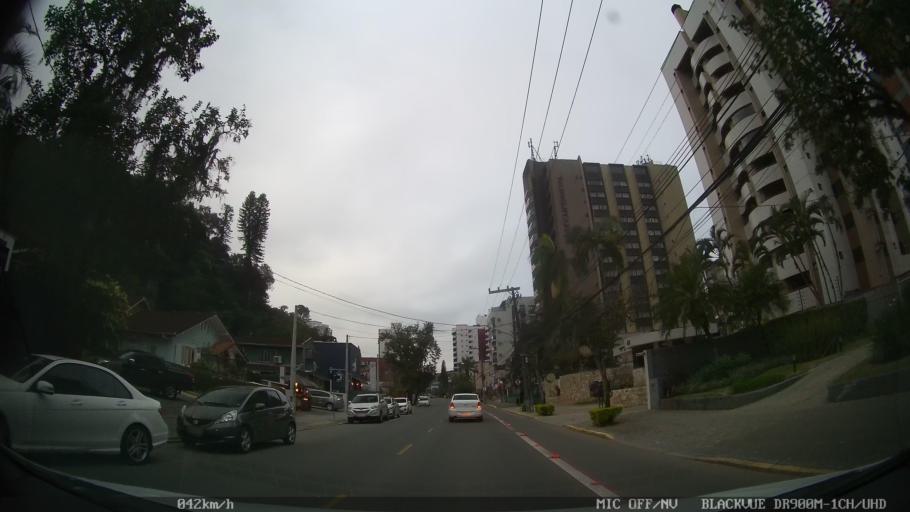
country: BR
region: Santa Catarina
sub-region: Joinville
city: Joinville
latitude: -26.3027
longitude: -48.8564
